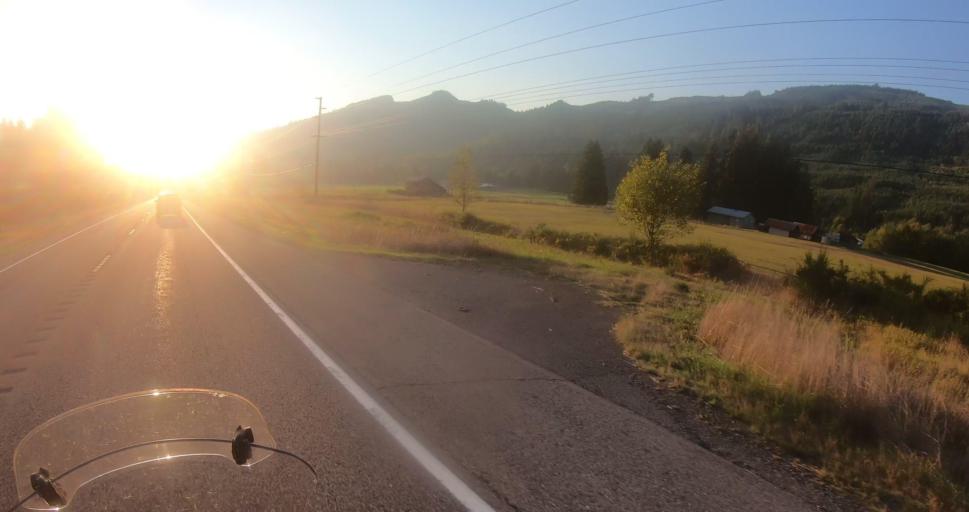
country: US
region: Washington
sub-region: Lewis County
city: Morton
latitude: 46.5388
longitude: -122.1031
